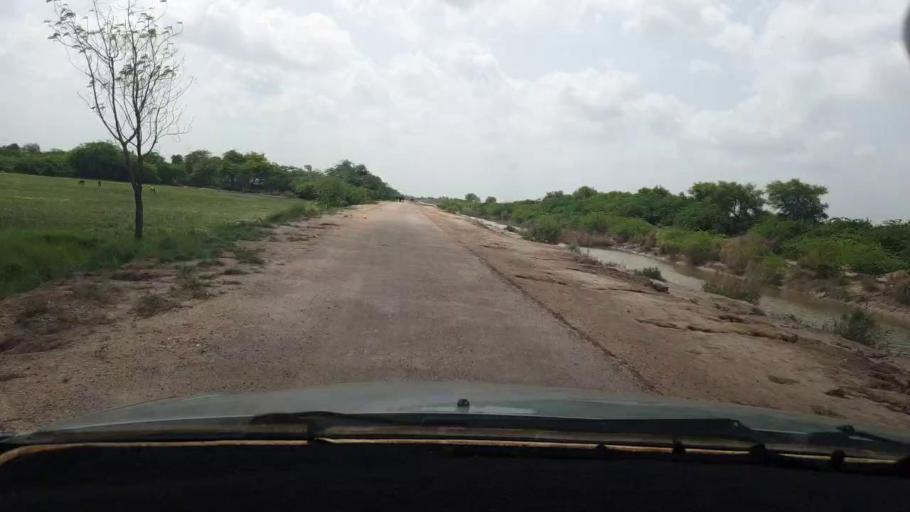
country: PK
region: Sindh
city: Tando Bago
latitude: 24.7257
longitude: 69.1349
